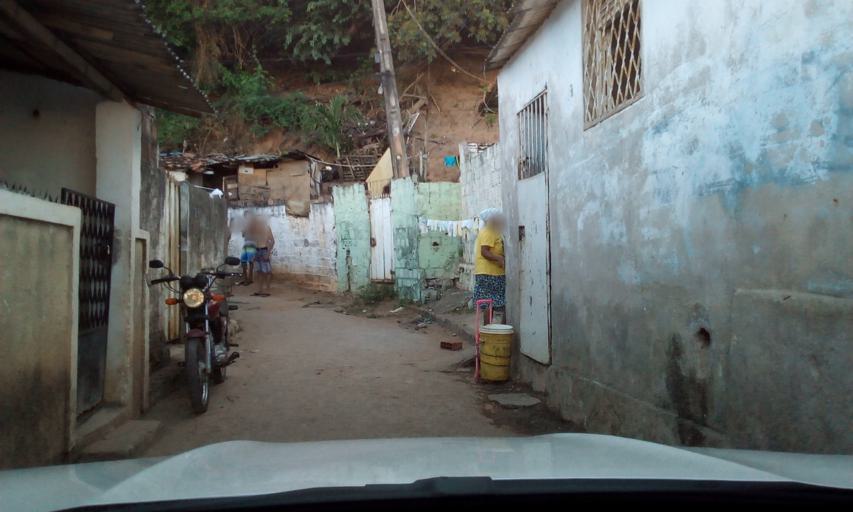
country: BR
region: Paraiba
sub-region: Joao Pessoa
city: Joao Pessoa
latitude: -7.1099
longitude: -34.8386
